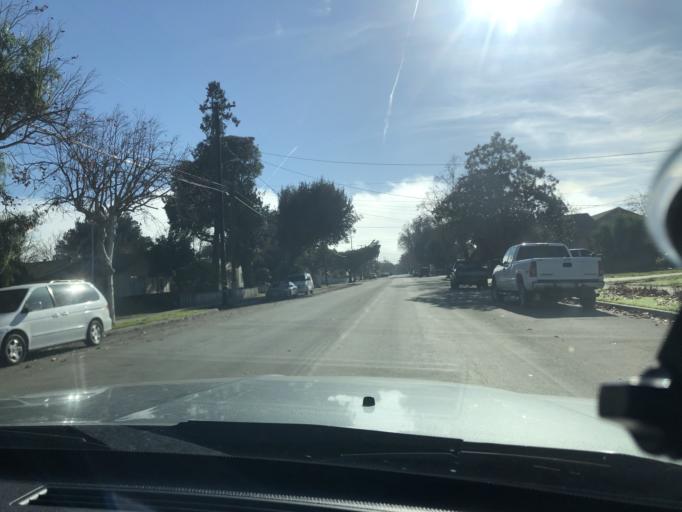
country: US
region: California
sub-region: Monterey County
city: King City
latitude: 36.2139
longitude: -121.1310
